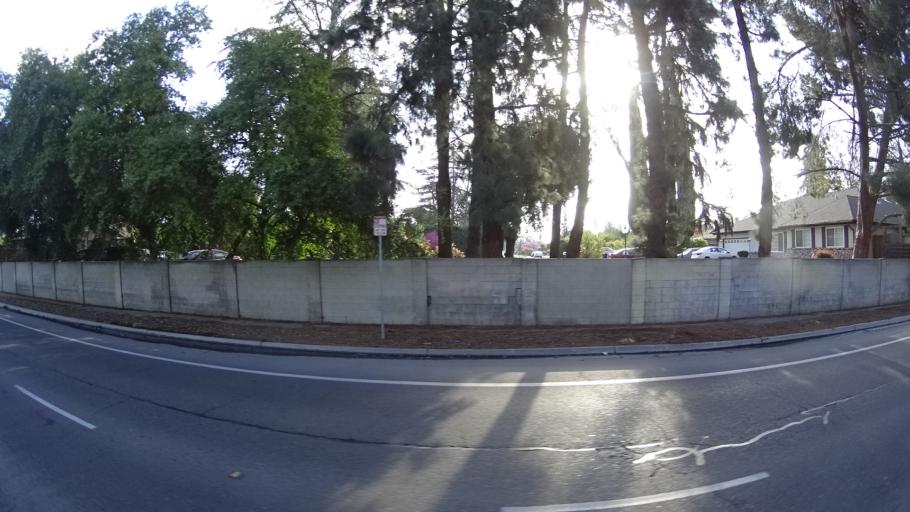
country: US
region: California
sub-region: Fresno County
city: Fresno
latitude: 36.8136
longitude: -119.8263
